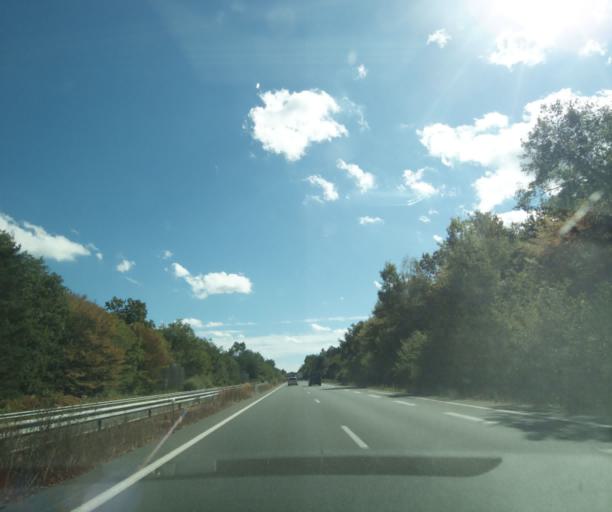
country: FR
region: Aquitaine
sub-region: Departement du Lot-et-Garonne
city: Fourques-sur-Garonne
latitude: 44.3993
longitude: 0.1900
